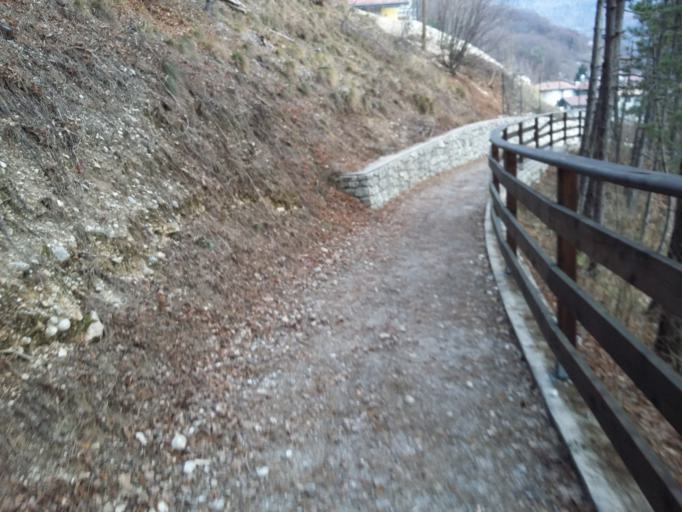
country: IT
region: Trentino-Alto Adige
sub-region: Provincia di Trento
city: Besenello
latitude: 45.9284
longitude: 11.1164
